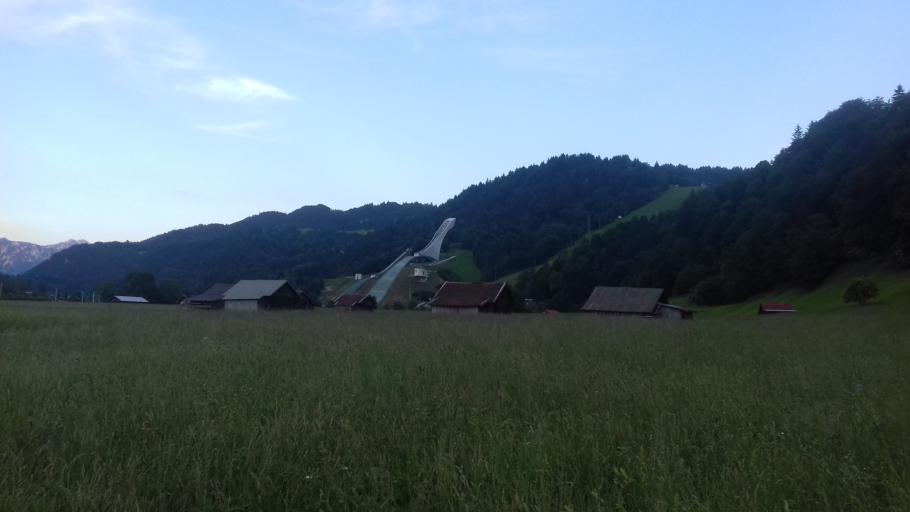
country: DE
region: Bavaria
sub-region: Upper Bavaria
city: Garmisch-Partenkirchen
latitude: 47.4834
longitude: 11.1062
